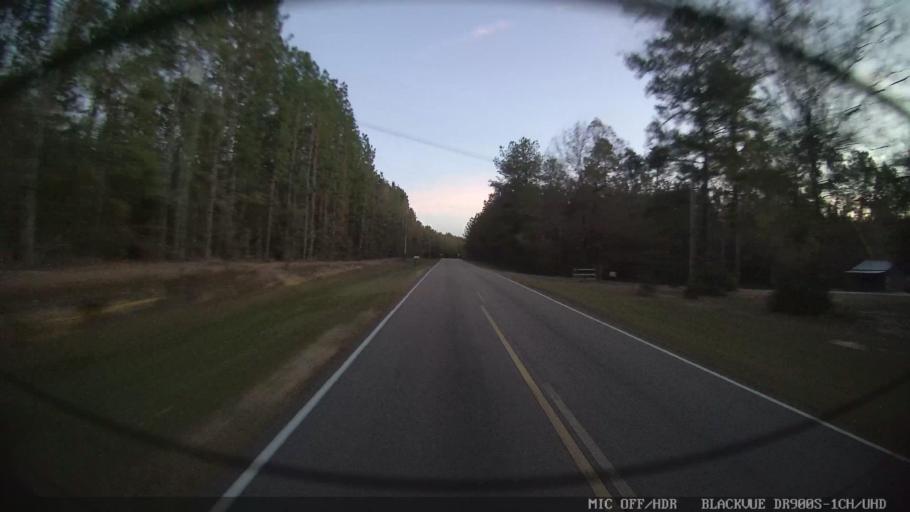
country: US
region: Mississippi
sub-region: Perry County
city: New Augusta
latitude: 31.1060
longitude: -89.1930
